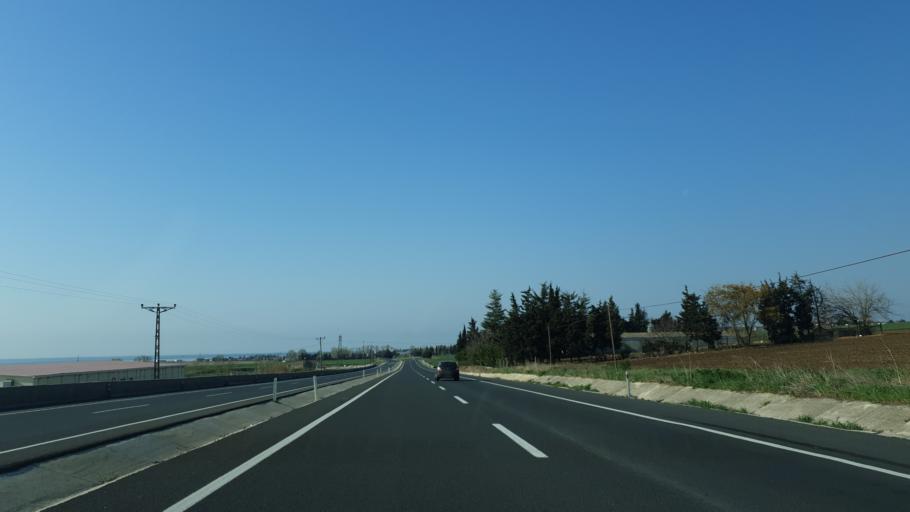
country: TR
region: Tekirdag
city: Corlu
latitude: 41.0294
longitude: 27.7262
